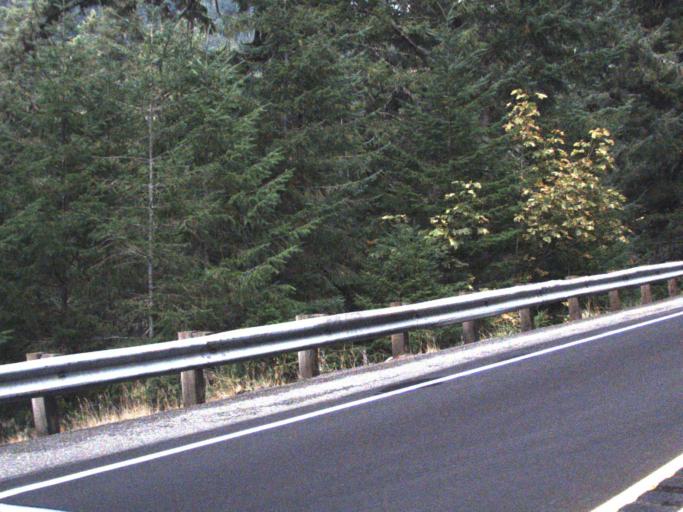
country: US
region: Washington
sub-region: Pierce County
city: Buckley
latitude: 46.6879
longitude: -121.5795
